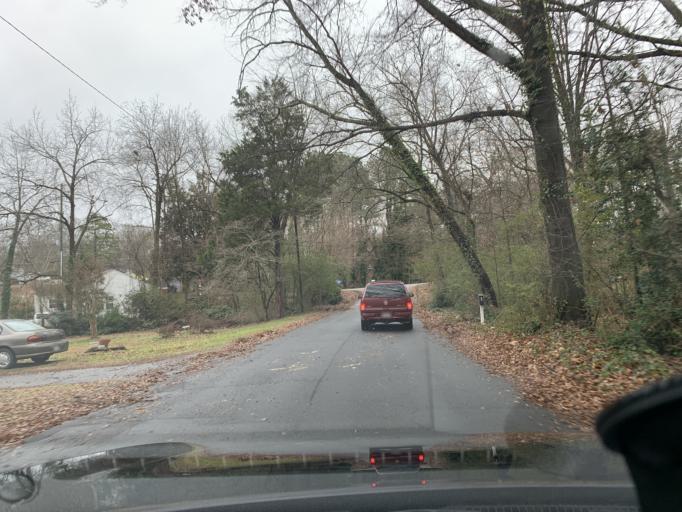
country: US
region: Georgia
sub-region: Cobb County
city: Marietta
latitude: 33.9490
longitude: -84.5031
